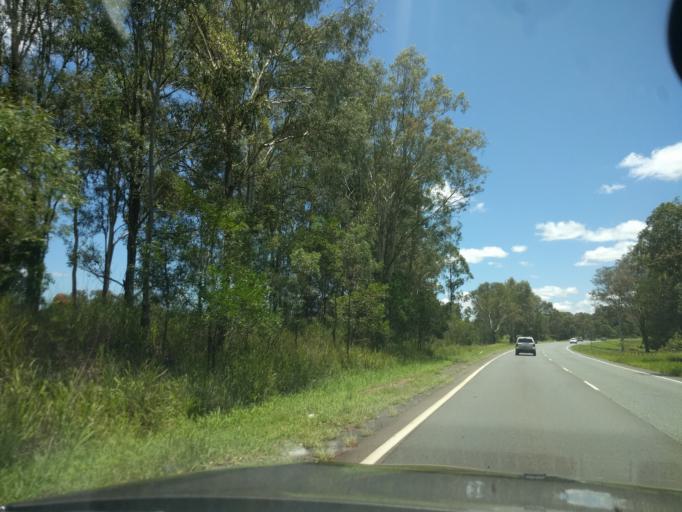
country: AU
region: Queensland
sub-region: Logan
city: Cedar Vale
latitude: -27.8603
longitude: 153.0024
